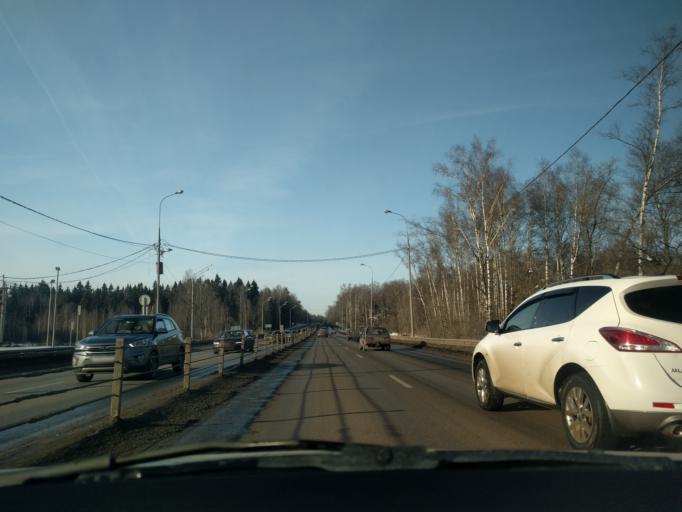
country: RU
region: Moskovskaya
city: Marfino
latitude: 56.0189
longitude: 37.5453
